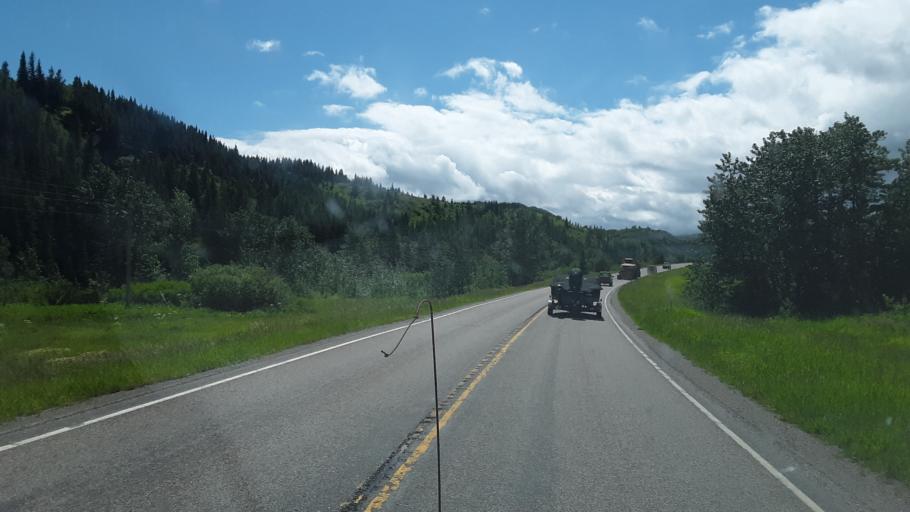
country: US
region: Montana
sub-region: Glacier County
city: South Browning
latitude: 48.3489
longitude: -113.3071
